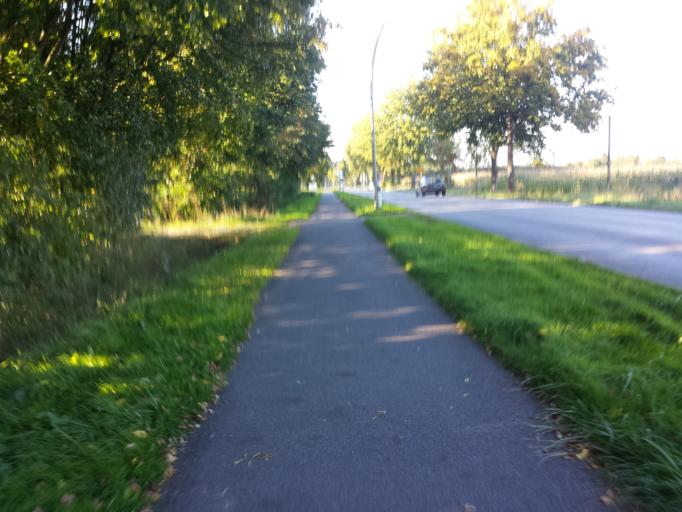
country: DE
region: North Rhine-Westphalia
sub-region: Regierungsbezirk Detmold
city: Langenberg
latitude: 51.7614
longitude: 8.3219
